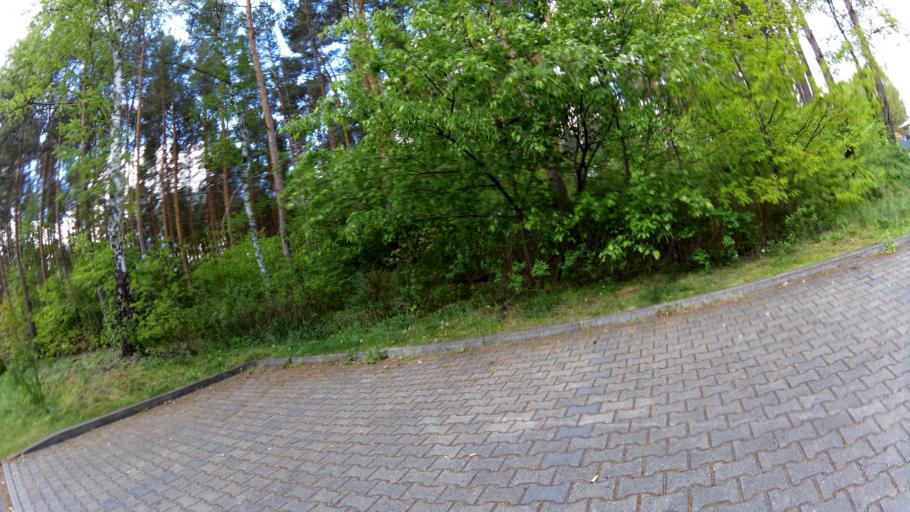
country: DE
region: Brandenburg
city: Halbe
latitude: 52.1056
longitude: 13.6938
